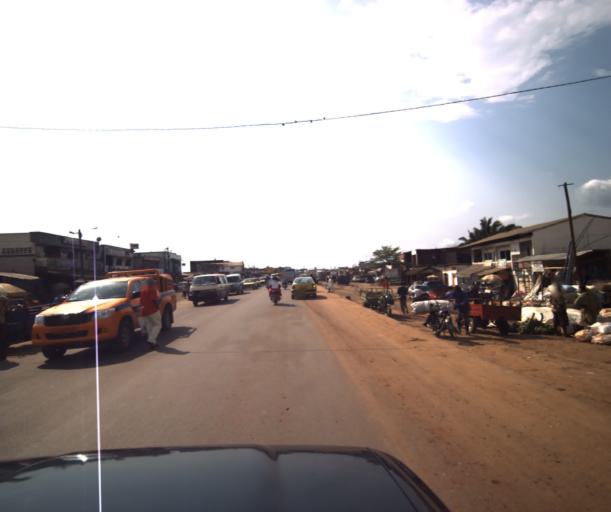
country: CM
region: Littoral
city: Douala
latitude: 4.0130
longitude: 9.7304
